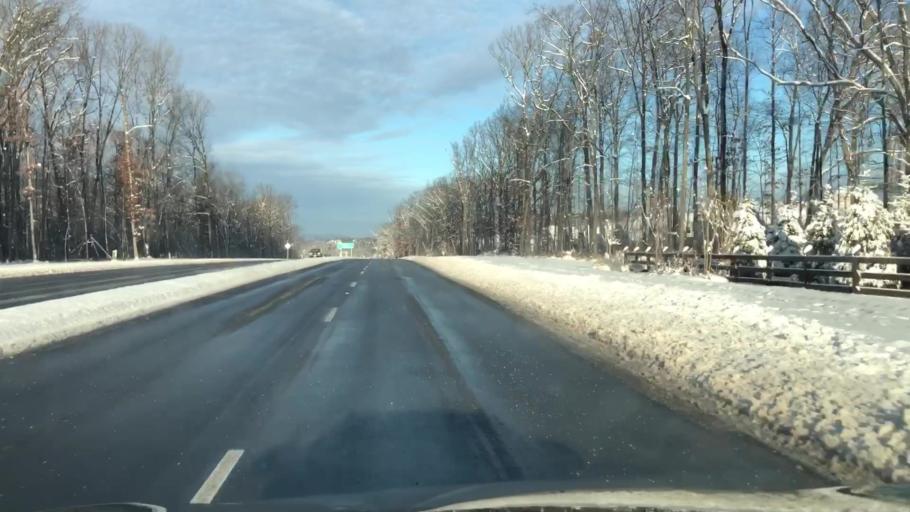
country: US
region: Virginia
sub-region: Prince William County
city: Linton Hall
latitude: 38.7279
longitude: -77.5575
